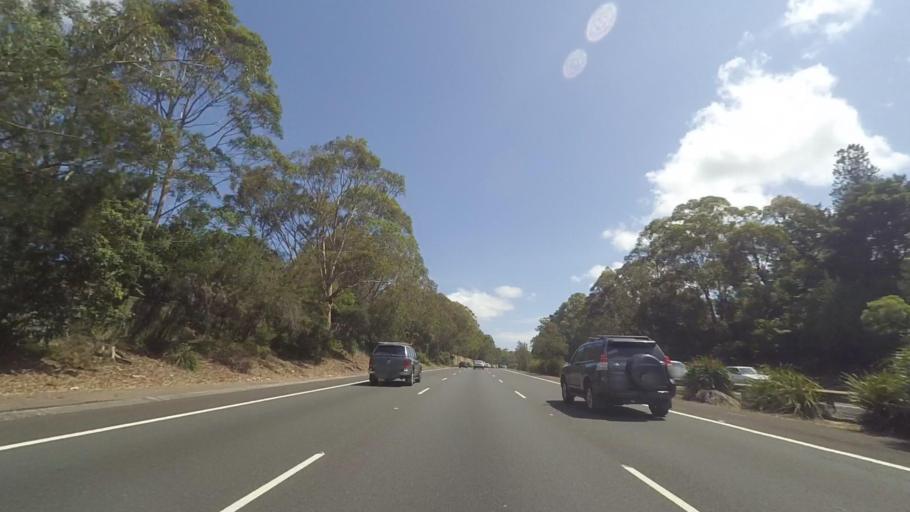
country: AU
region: New South Wales
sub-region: Ku-ring-gai
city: North Wahroonga
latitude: -33.7094
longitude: 151.1169
